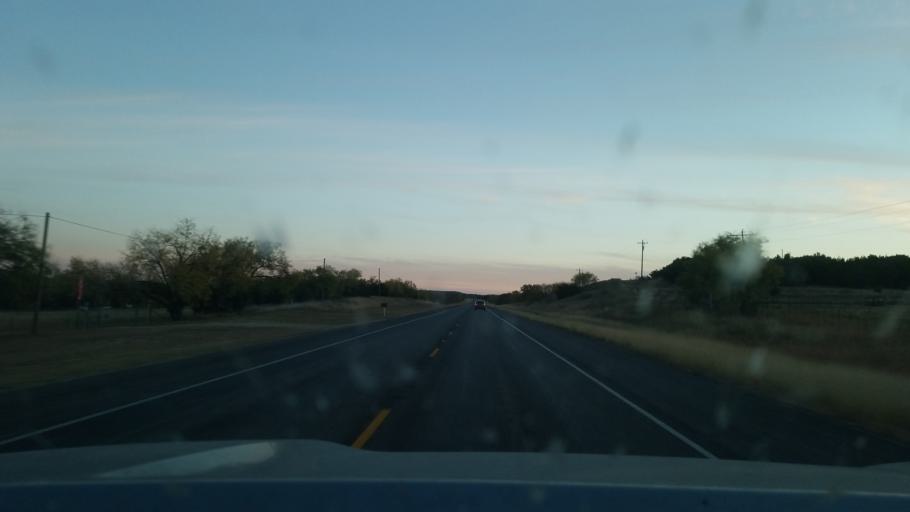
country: US
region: Texas
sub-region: Stephens County
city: Breckenridge
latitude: 32.5957
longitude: -98.8992
